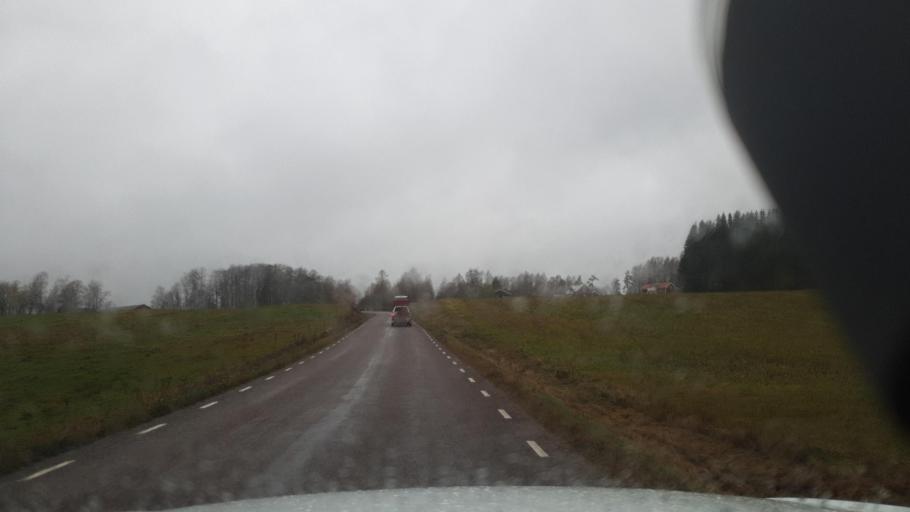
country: SE
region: Vaermland
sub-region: Sunne Kommun
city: Sunne
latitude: 59.7392
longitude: 13.1193
